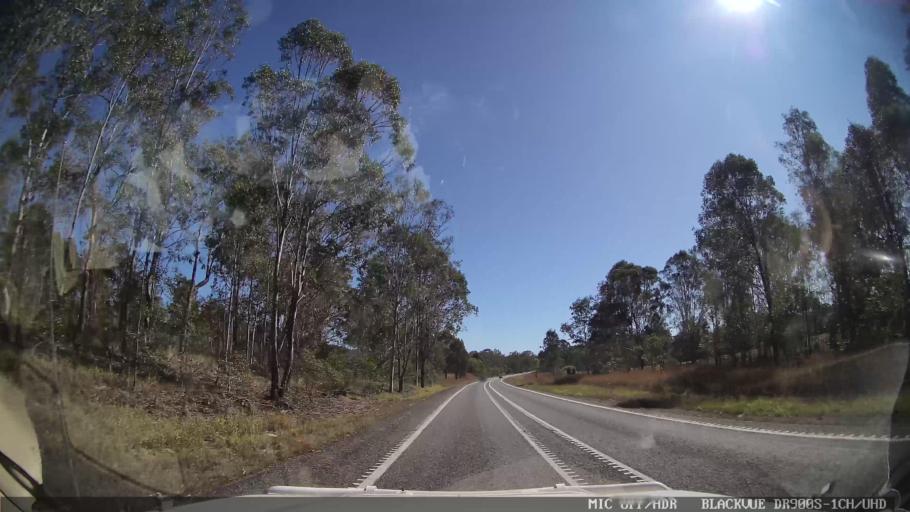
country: AU
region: Queensland
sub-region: Gympie Regional Council
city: Gympie
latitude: -26.0460
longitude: 152.5739
